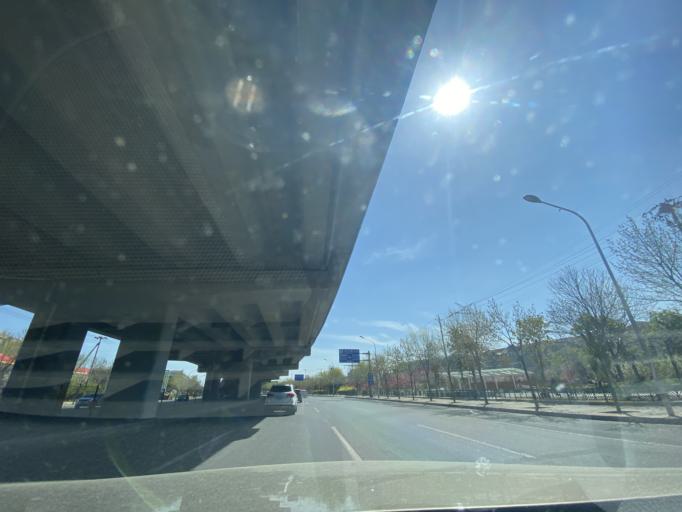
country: CN
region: Beijing
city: Babaoshan
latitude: 39.9231
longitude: 116.2506
